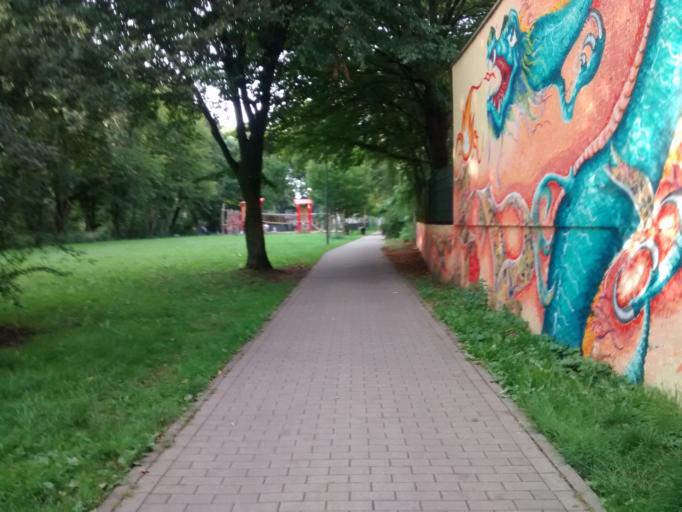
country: DE
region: North Rhine-Westphalia
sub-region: Regierungsbezirk Koln
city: Merheim
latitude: 50.9701
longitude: 7.0445
